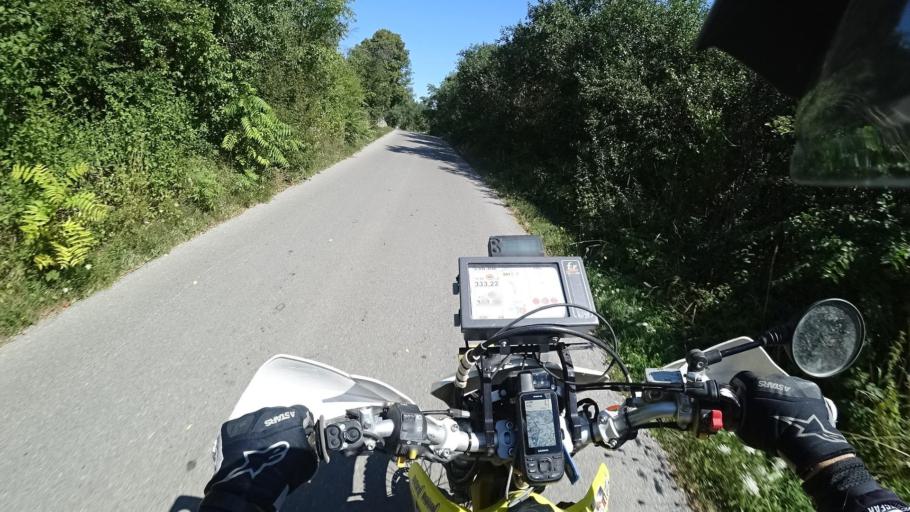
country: HR
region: Licko-Senjska
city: Popovaca
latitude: 44.7153
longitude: 15.2683
